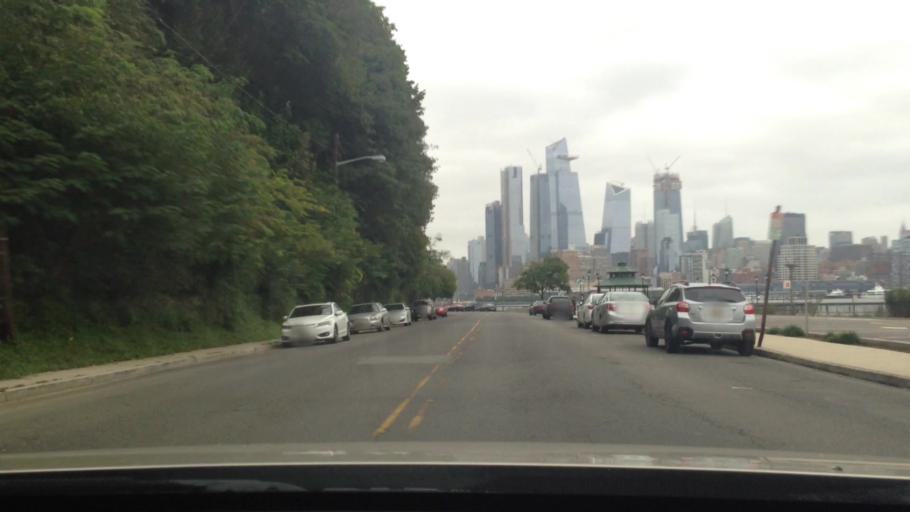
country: US
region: New Jersey
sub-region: Hudson County
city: Hoboken
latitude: 40.7434
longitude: -74.0247
